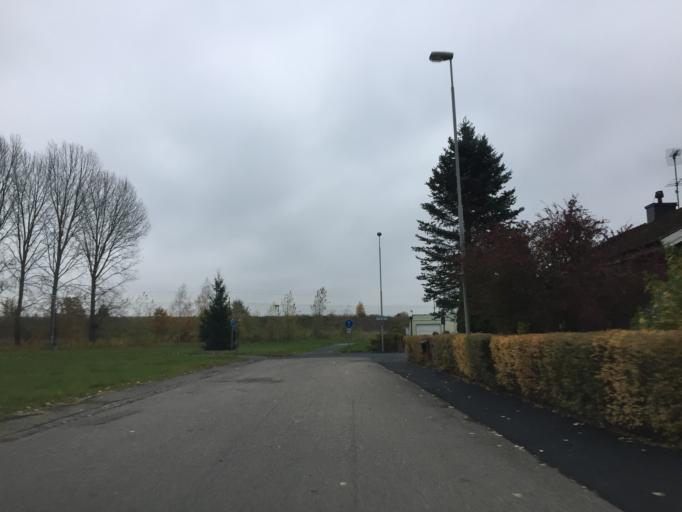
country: SE
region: Vaestra Goetaland
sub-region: Trollhattan
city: Trollhattan
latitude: 58.2697
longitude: 12.3128
